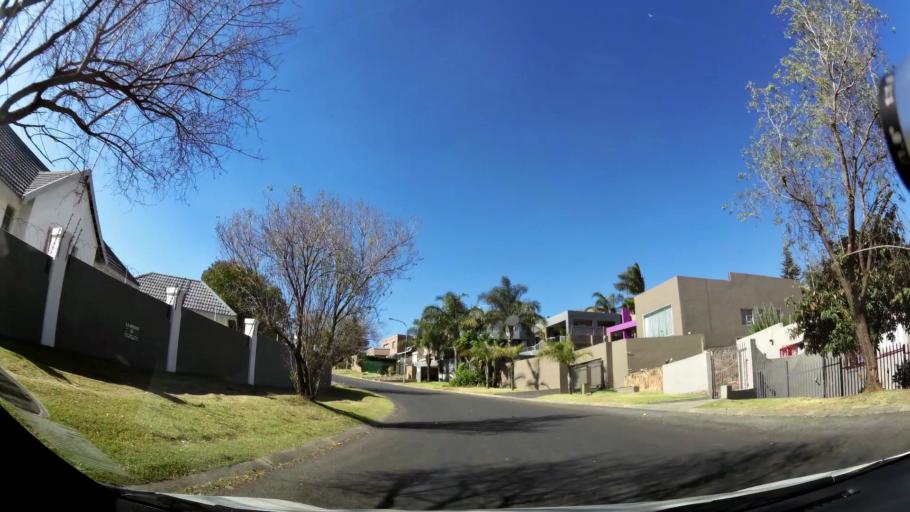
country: ZA
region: Gauteng
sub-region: City of Johannesburg Metropolitan Municipality
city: Johannesburg
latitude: -26.2630
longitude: 27.9959
